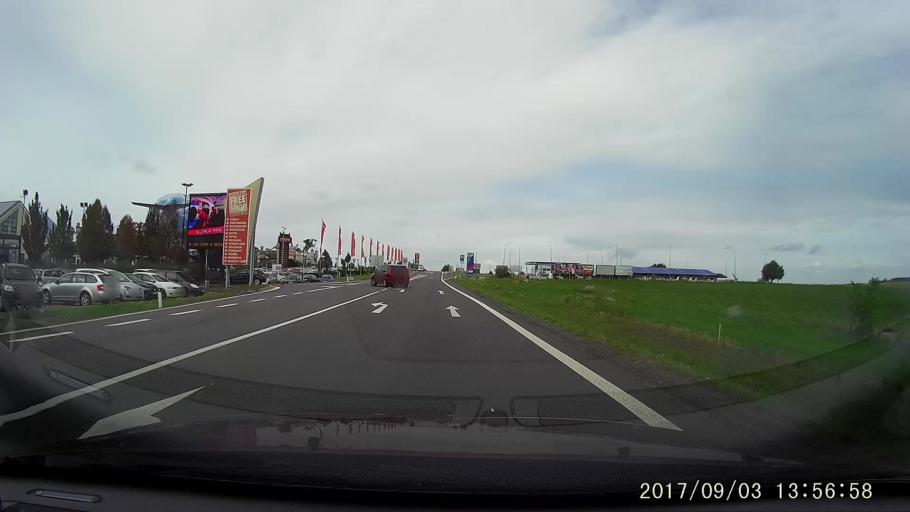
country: CZ
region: South Moravian
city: Vrbovec
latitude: 48.7632
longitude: 16.0655
